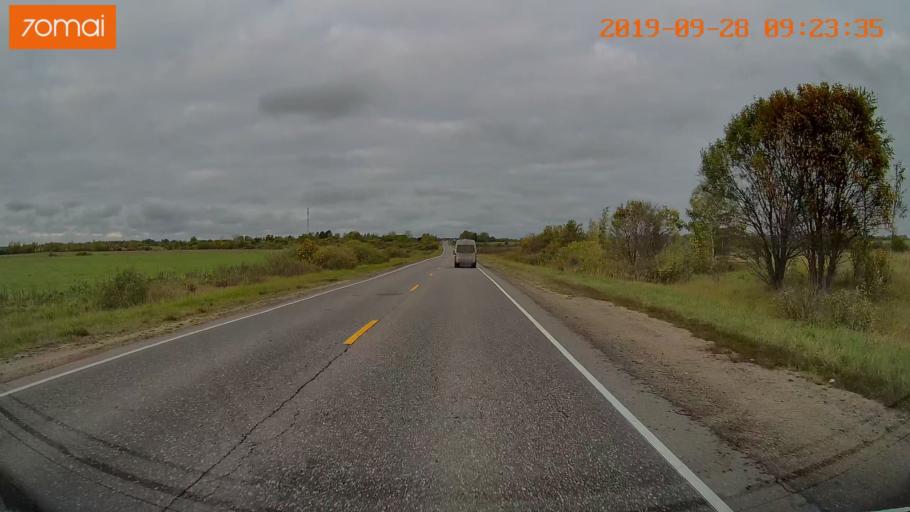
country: RU
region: Jaroslavl
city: Dubki
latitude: 57.1959
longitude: 40.3525
